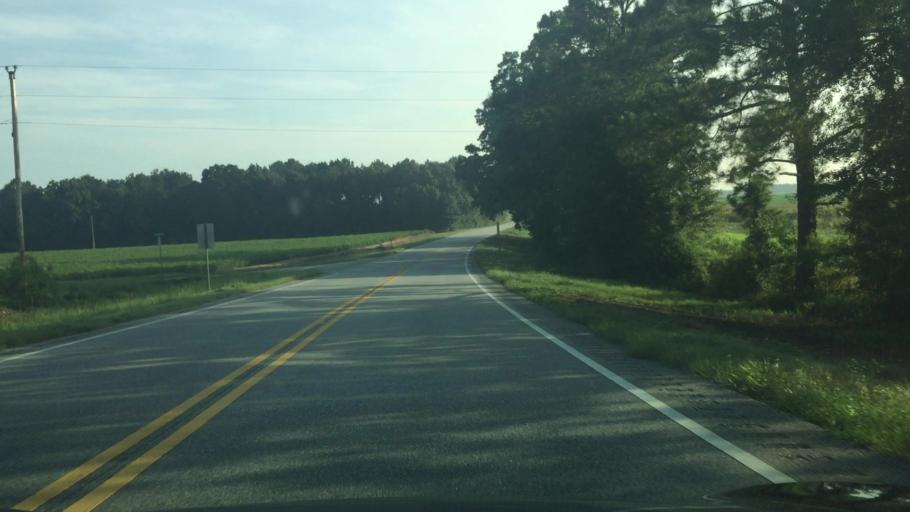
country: US
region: Alabama
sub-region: Covington County
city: Andalusia
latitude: 31.1715
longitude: -86.4599
